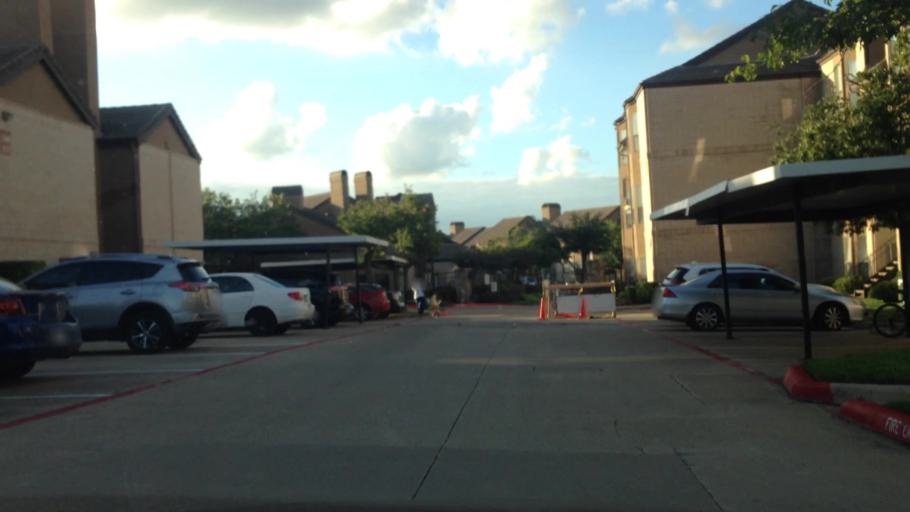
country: US
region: Texas
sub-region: Dallas County
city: Irving
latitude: 32.8804
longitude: -96.9711
